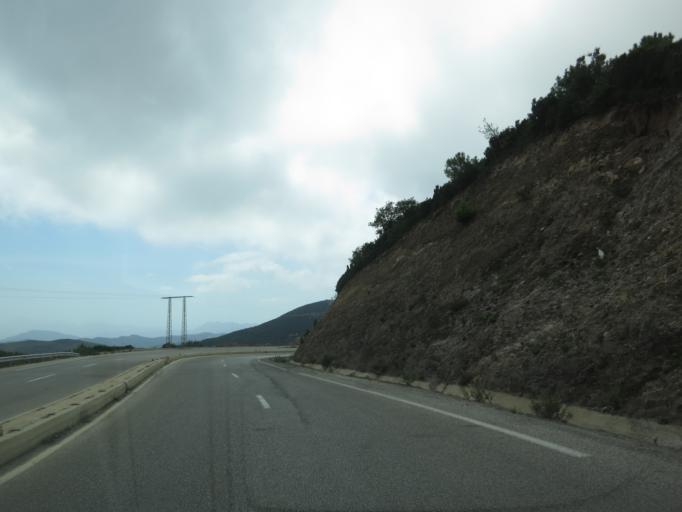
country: ES
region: Ceuta
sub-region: Ceuta
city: Ceuta
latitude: 35.8752
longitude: -5.4034
